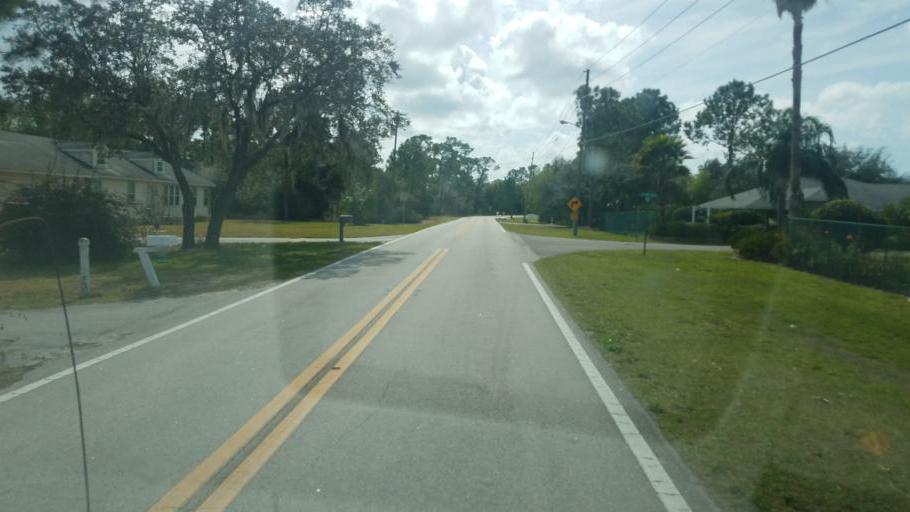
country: US
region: Florida
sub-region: Polk County
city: Dundee
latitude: 27.9994
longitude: -81.5255
